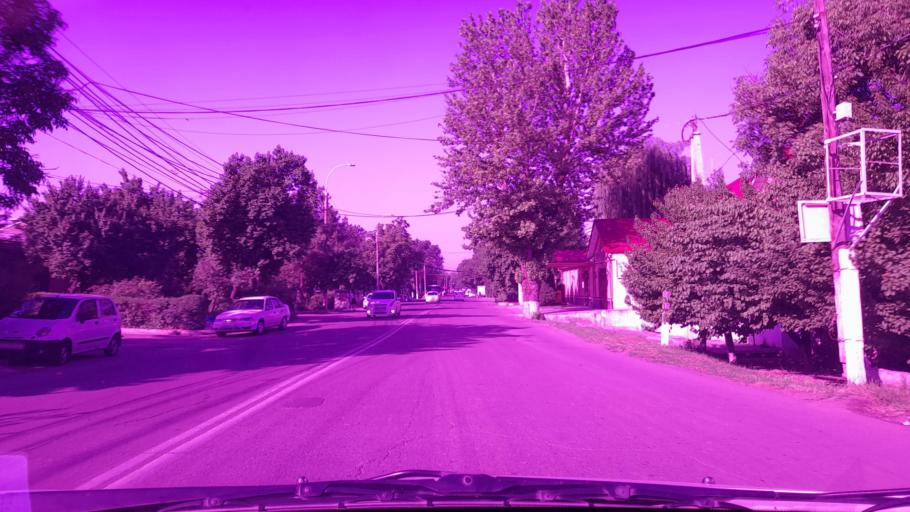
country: UZ
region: Toshkent
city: Salor
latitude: 41.3233
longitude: 69.3467
